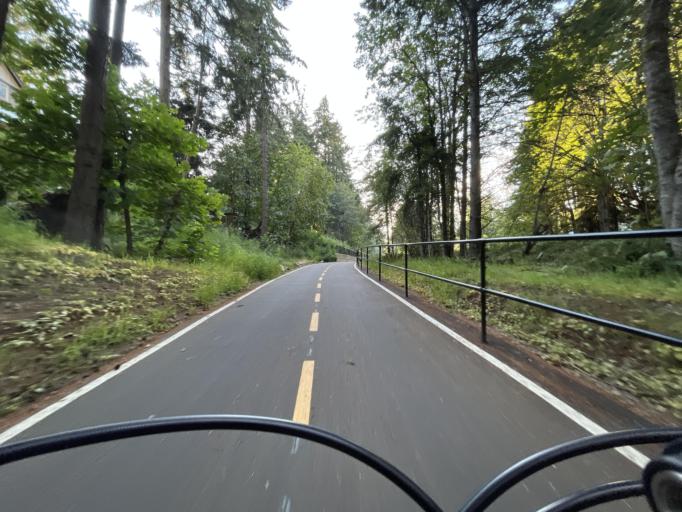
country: CA
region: British Columbia
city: Colwood
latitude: 48.4475
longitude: -123.4804
